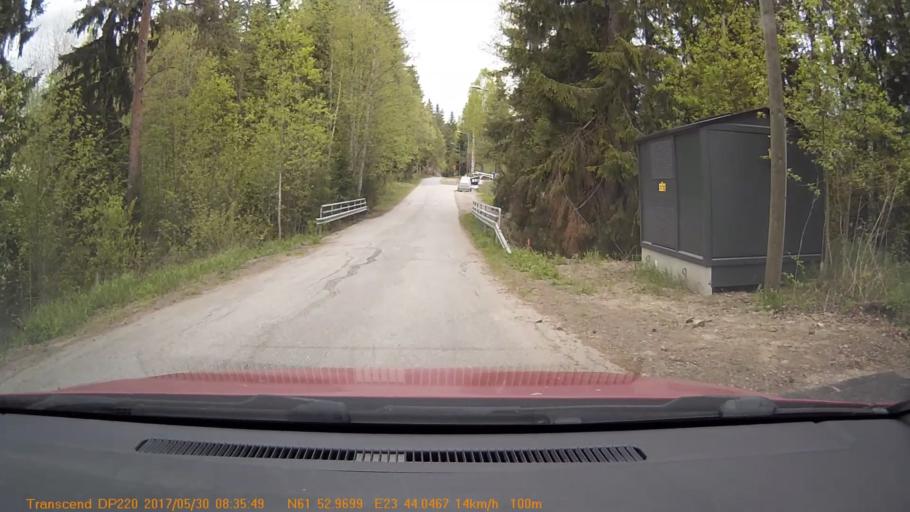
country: FI
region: Pirkanmaa
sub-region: Tampere
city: Kuru
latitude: 61.8829
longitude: 23.7341
